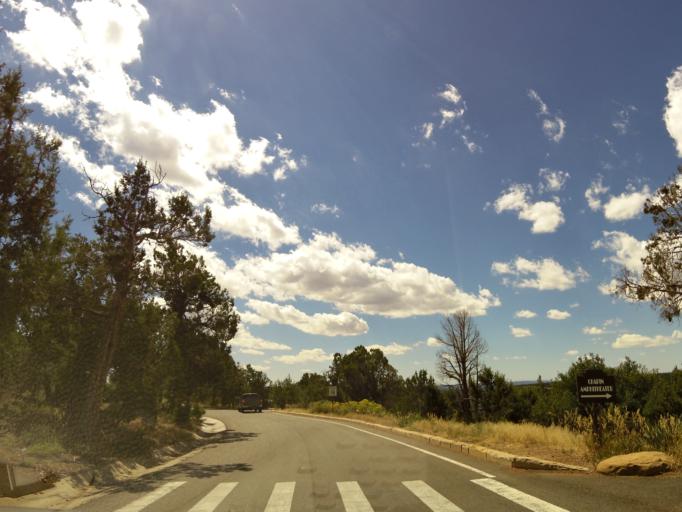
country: US
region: Colorado
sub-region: Montezuma County
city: Cortez
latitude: 37.1840
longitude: -108.4904
